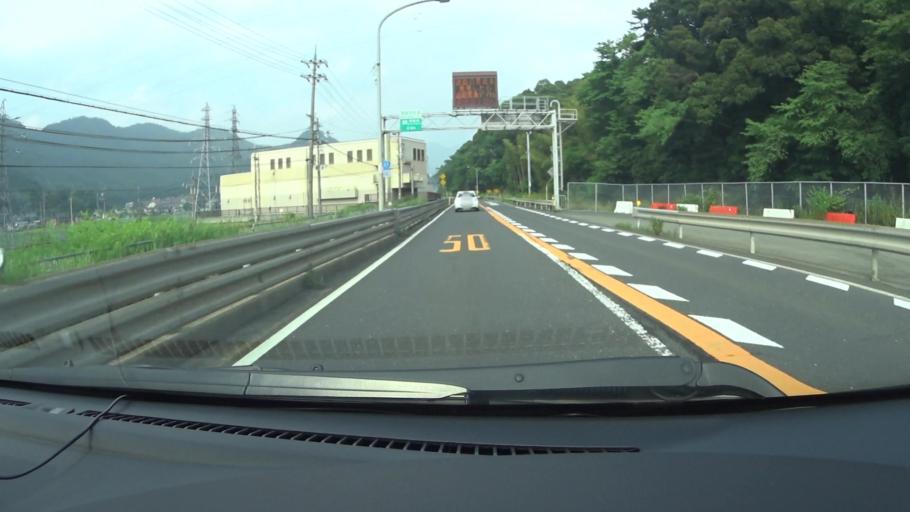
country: JP
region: Kyoto
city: Kameoka
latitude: 34.9992
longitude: 135.5732
